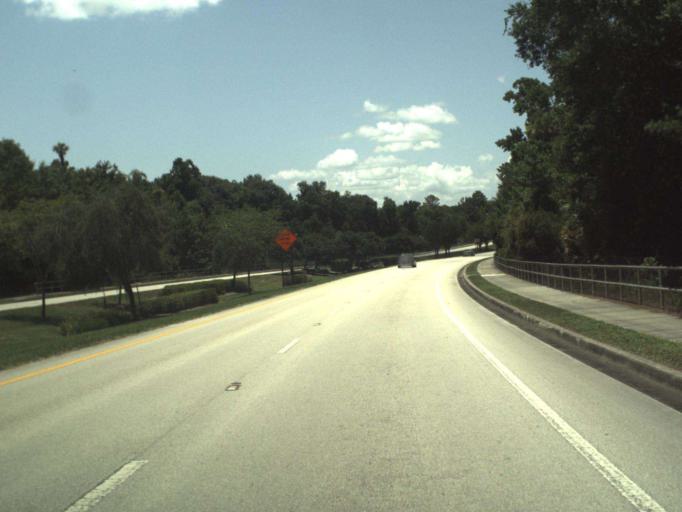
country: US
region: Florida
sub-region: Seminole County
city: Oviedo
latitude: 28.6910
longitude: -81.2560
